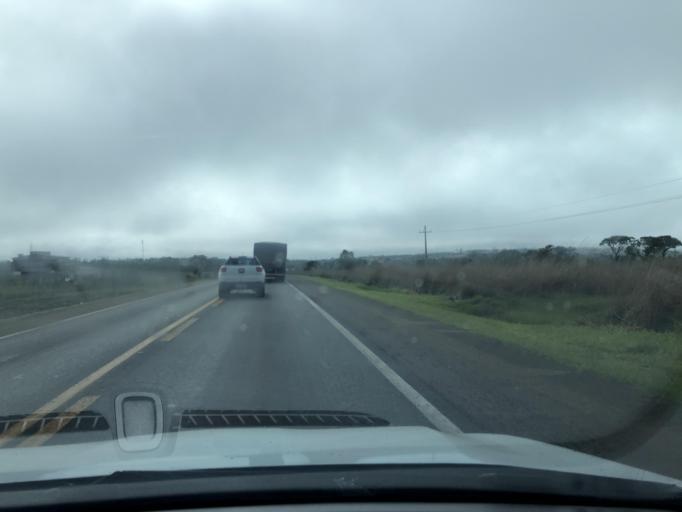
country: BR
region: Goias
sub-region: Cristalina
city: Cristalina
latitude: -16.7300
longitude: -47.6282
